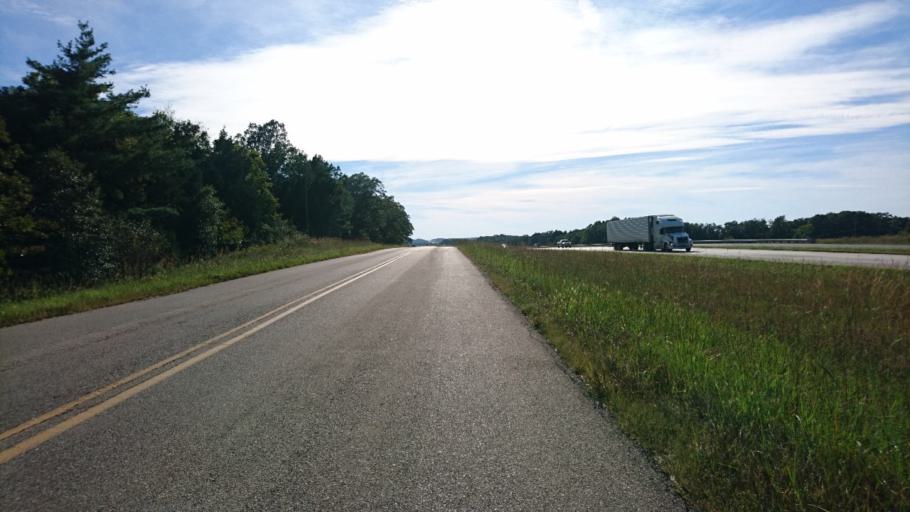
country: US
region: Missouri
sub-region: Crawford County
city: Bourbon
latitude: 38.1149
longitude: -91.3249
